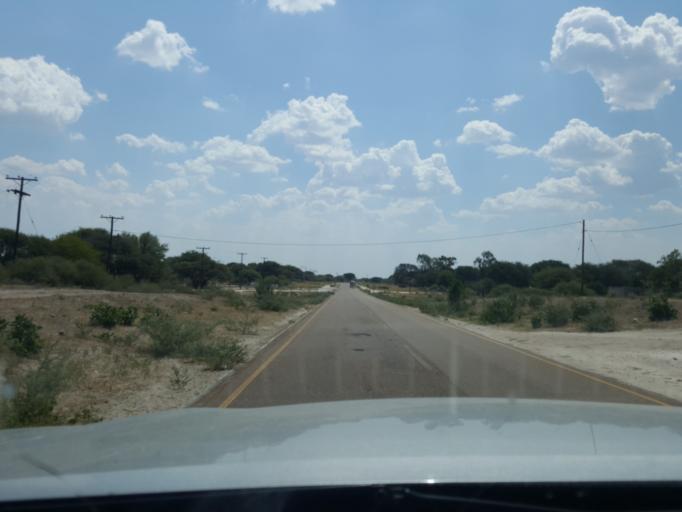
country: BW
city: Nokaneng
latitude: -19.6605
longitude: 22.1848
